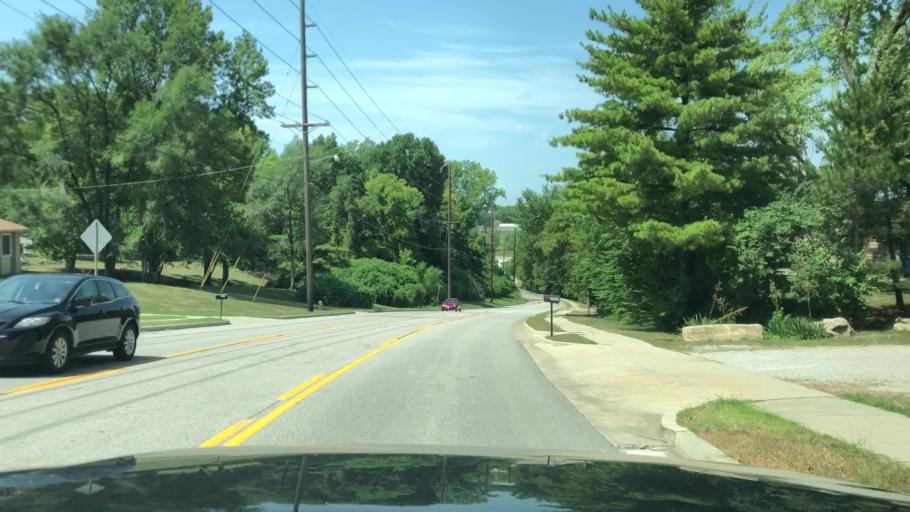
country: US
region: Missouri
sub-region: Saint Charles County
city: Saint Charles
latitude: 38.8063
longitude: -90.5467
